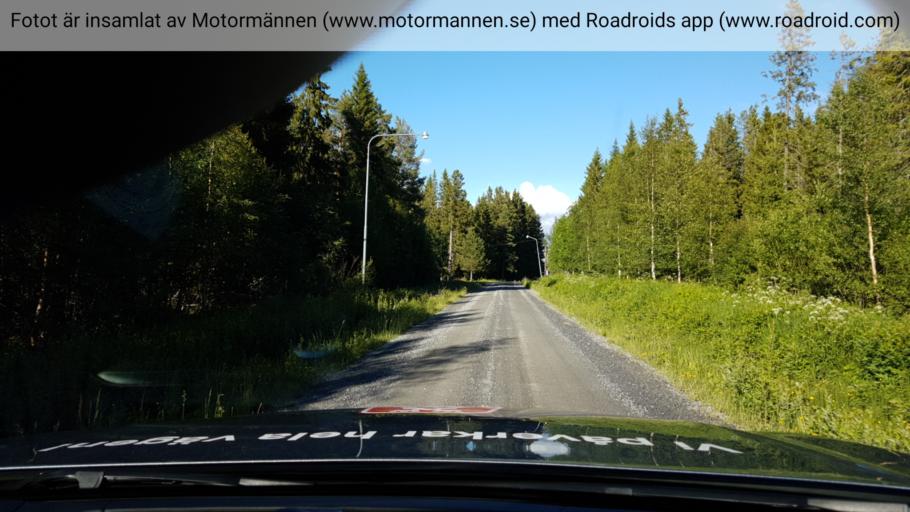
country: SE
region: Jaemtland
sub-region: Bergs Kommun
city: Hoverberg
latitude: 63.0286
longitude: 14.3885
